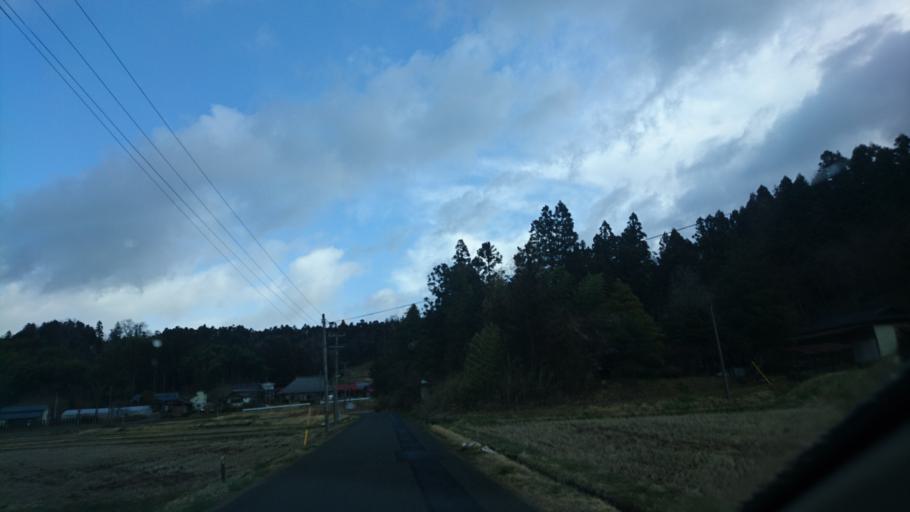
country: JP
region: Iwate
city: Ichinoseki
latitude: 38.7889
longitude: 141.0346
